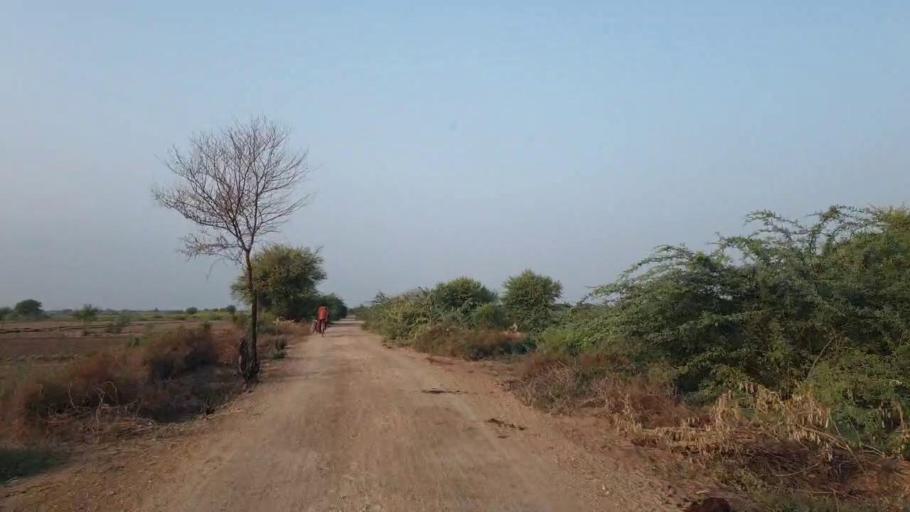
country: PK
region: Sindh
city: Tando Ghulam Ali
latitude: 25.0546
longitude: 68.9604
